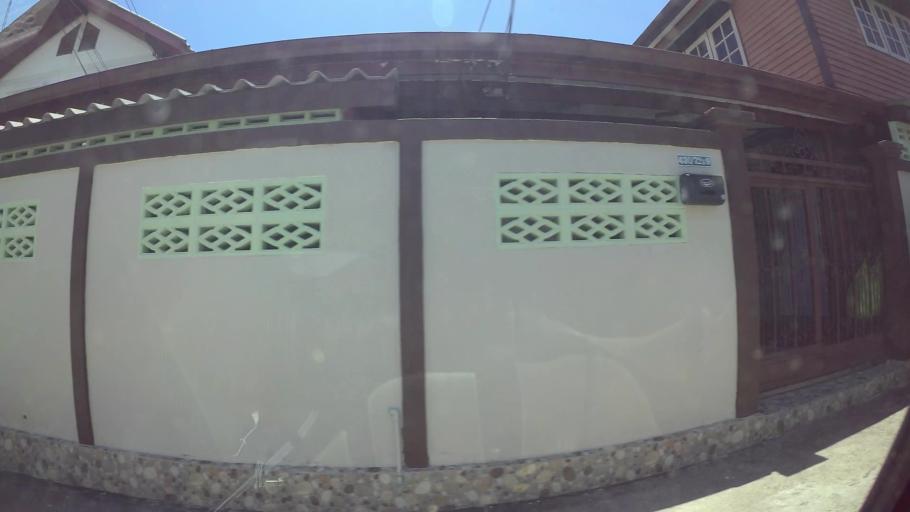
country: TH
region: Chon Buri
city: Phatthaya
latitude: 12.9304
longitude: 100.8958
